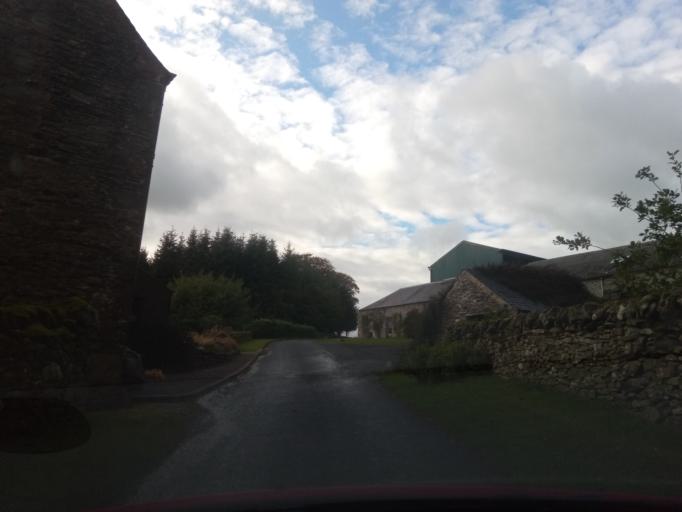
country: GB
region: Scotland
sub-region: The Scottish Borders
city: Galashiels
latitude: 55.6763
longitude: -2.8283
